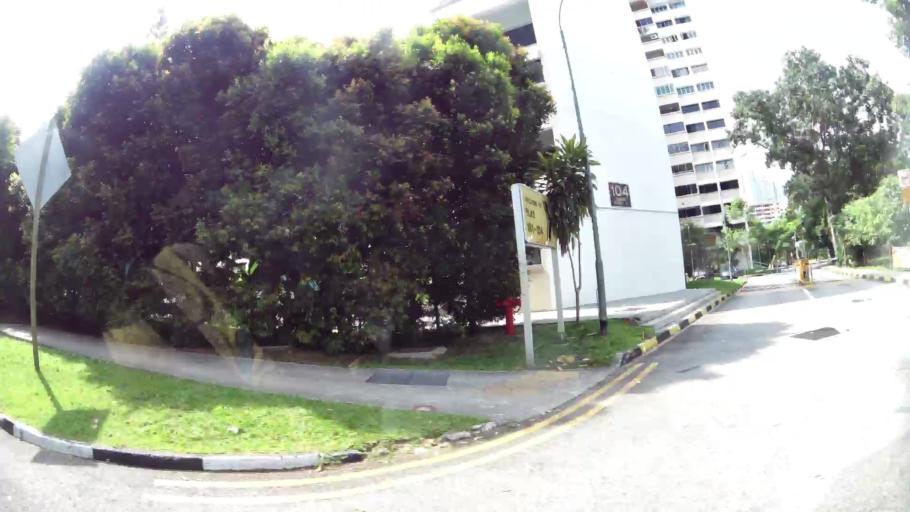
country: SG
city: Singapore
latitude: 1.3233
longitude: 103.7690
